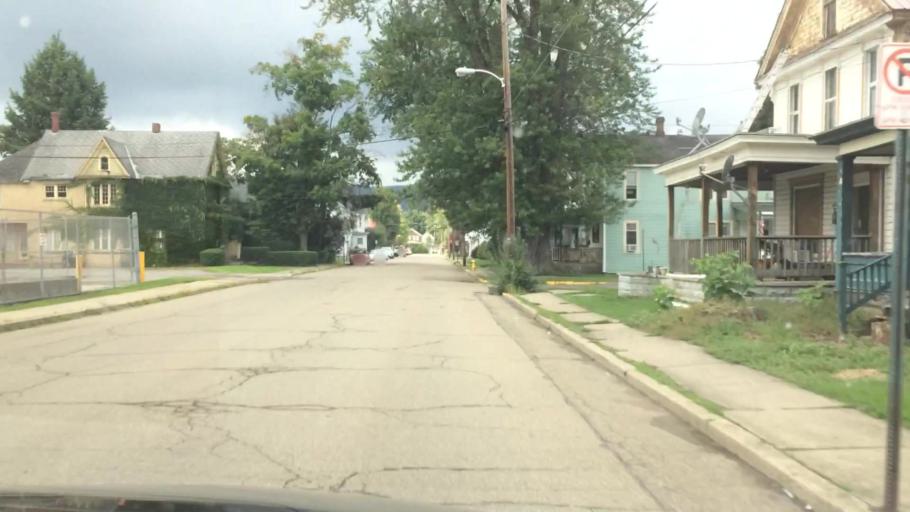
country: US
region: Pennsylvania
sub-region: McKean County
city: Bradford
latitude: 41.9581
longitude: -78.6456
